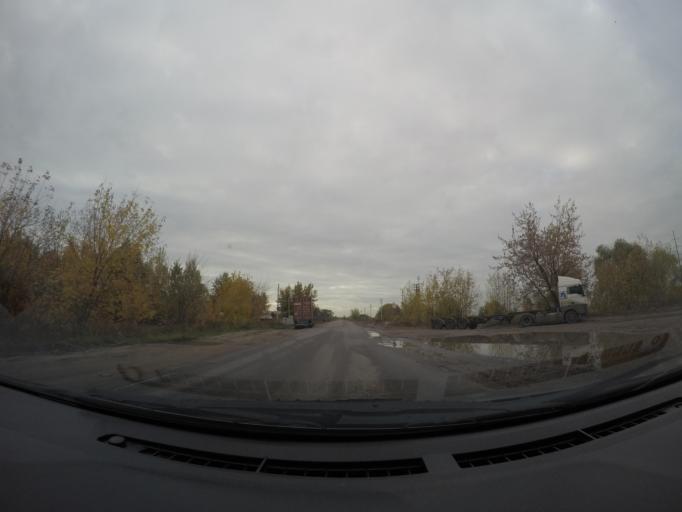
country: RU
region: Moskovskaya
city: Staraya Kupavna
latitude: 55.7802
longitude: 38.1860
